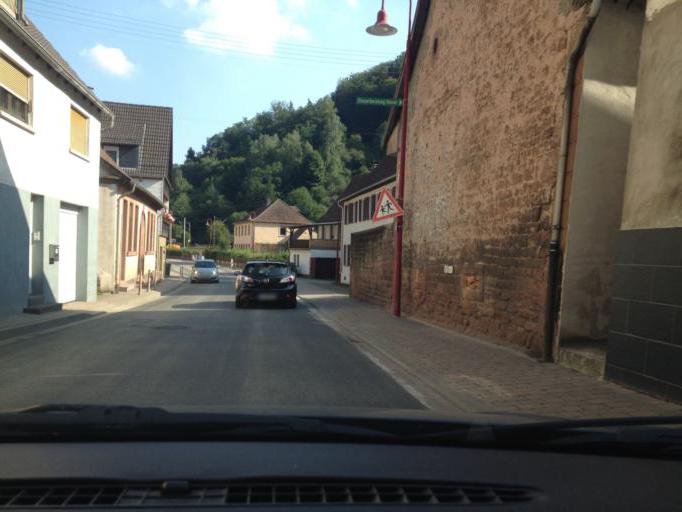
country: DE
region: Rheinland-Pfalz
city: Frankenstein
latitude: 49.4396
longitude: 7.9766
